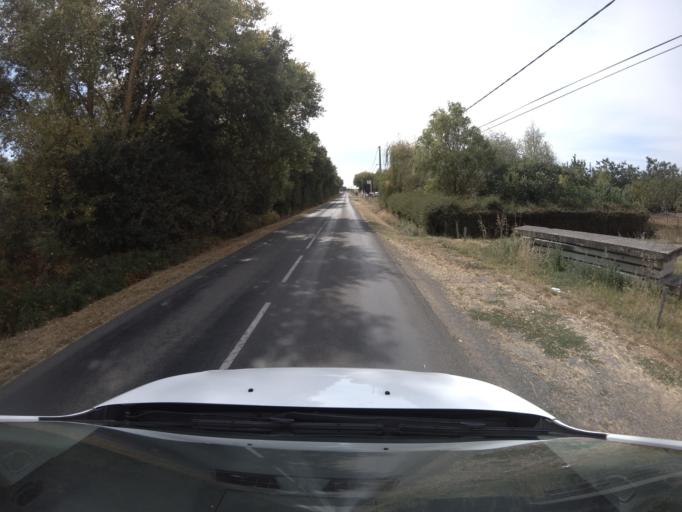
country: FR
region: Poitou-Charentes
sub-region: Departement des Deux-Sevres
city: Saint-Leger-de-Montbrun
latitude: 46.9932
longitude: -0.1310
